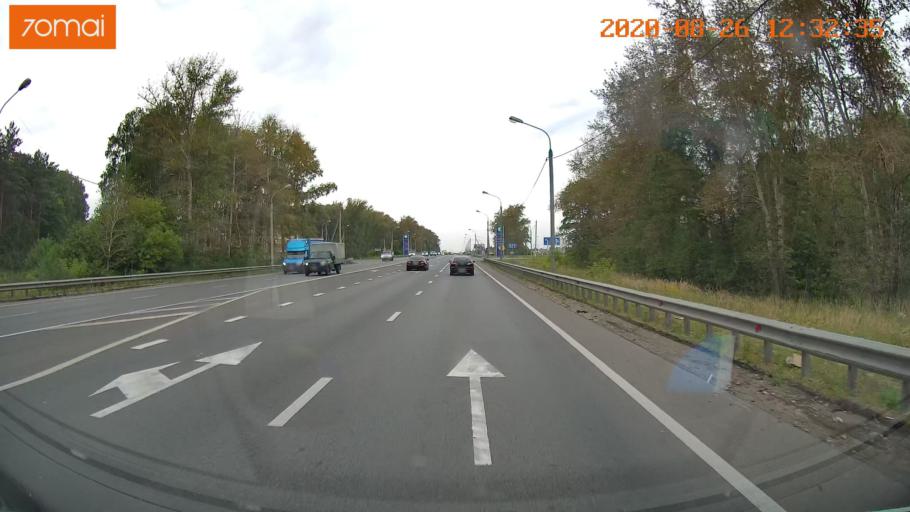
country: RU
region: Rjazan
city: Ryazan'
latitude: 54.5781
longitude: 39.7880
